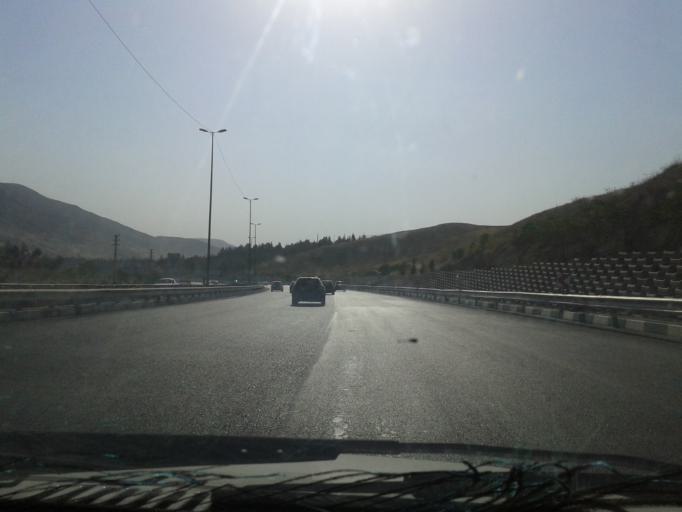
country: IR
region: Tehran
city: Tehran
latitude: 35.7300
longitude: 51.6258
